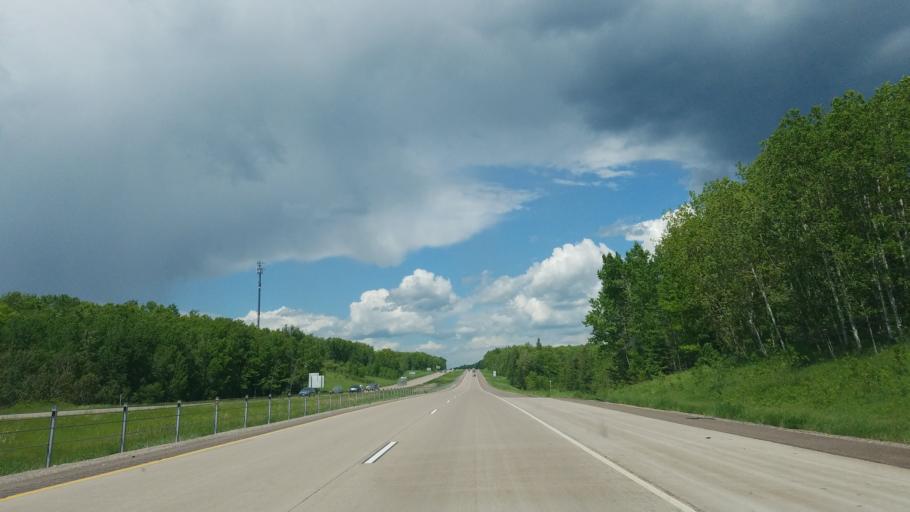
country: US
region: Minnesota
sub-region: Carlton County
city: Moose Lake
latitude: 46.4552
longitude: -92.7280
